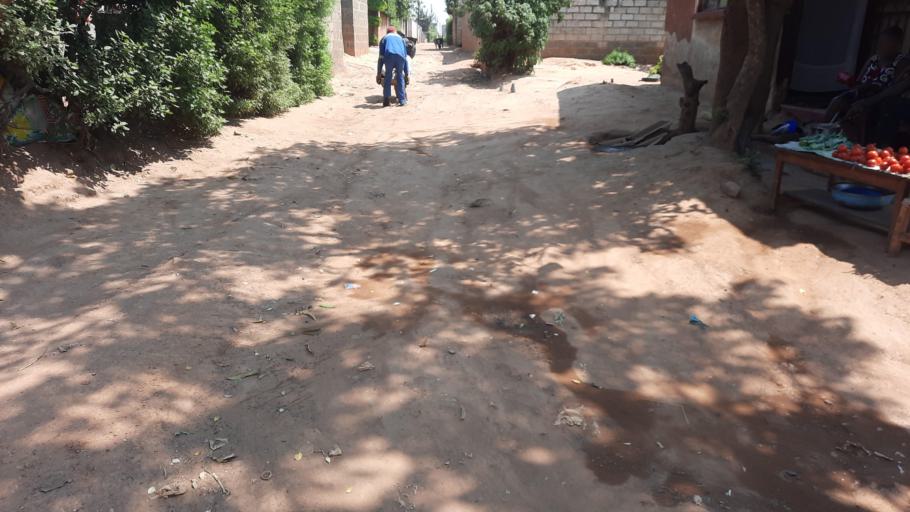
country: ZM
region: Lusaka
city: Lusaka
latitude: -15.3982
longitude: 28.3748
